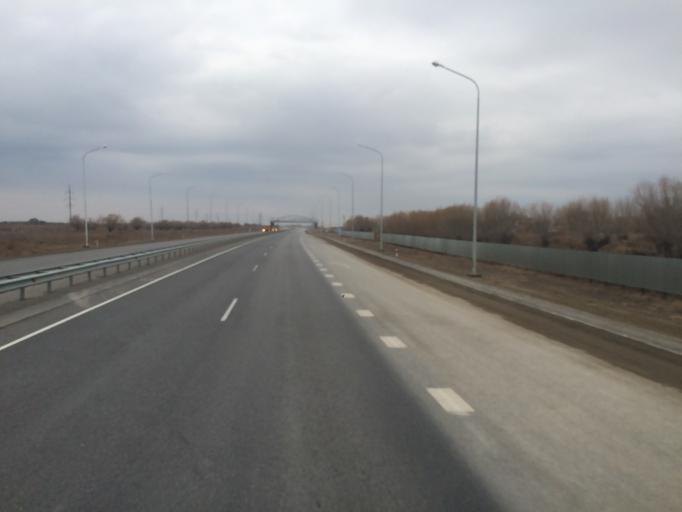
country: KZ
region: Qyzylorda
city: Shieli
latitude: 44.1352
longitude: 66.9729
